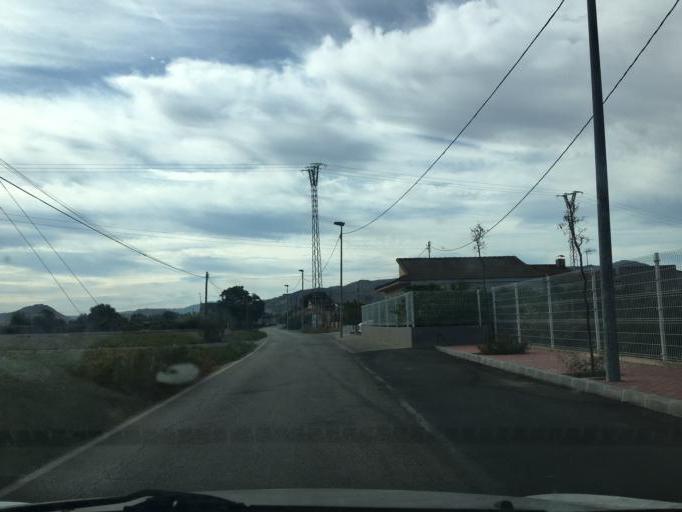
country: ES
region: Murcia
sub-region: Murcia
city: Santomera
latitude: 38.0147
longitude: -1.0459
